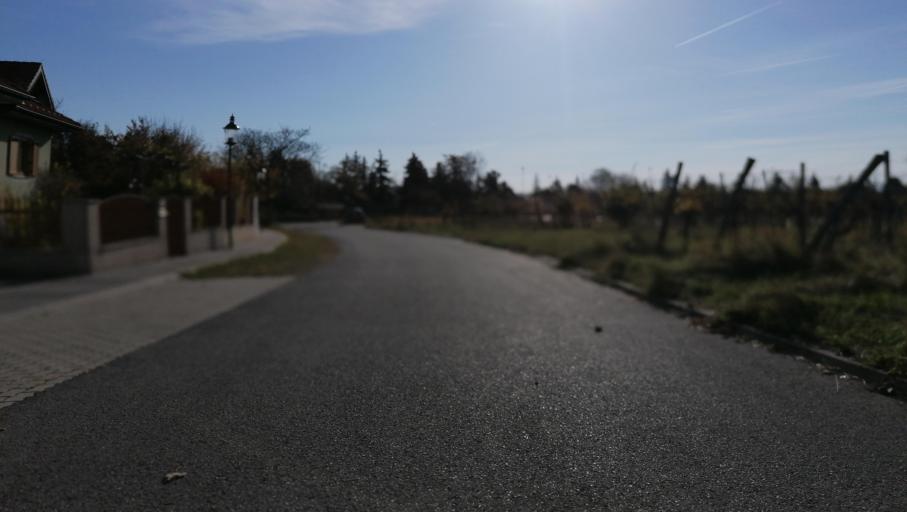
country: AT
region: Lower Austria
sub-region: Politischer Bezirk Modling
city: Gumpoldskirchen
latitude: 48.0396
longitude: 16.2799
